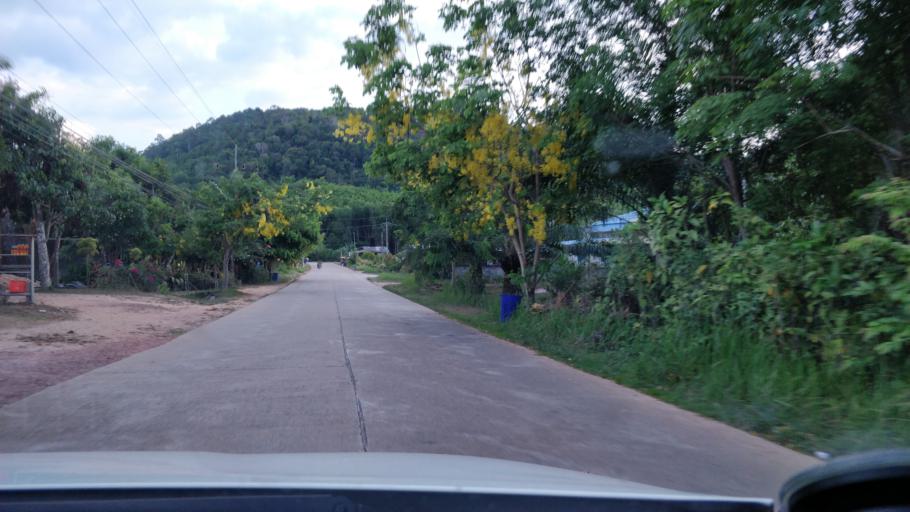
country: TH
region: Krabi
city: Saladan
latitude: 7.5836
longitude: 99.0679
